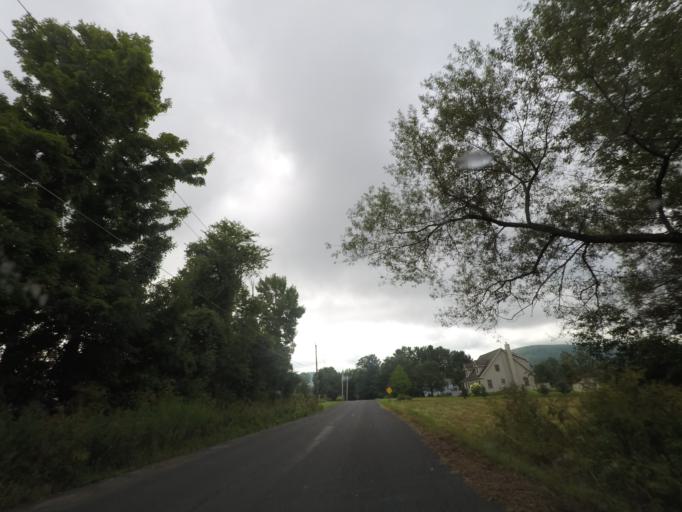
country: US
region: Massachusetts
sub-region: Berkshire County
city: Richmond
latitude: 42.4262
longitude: -73.3163
